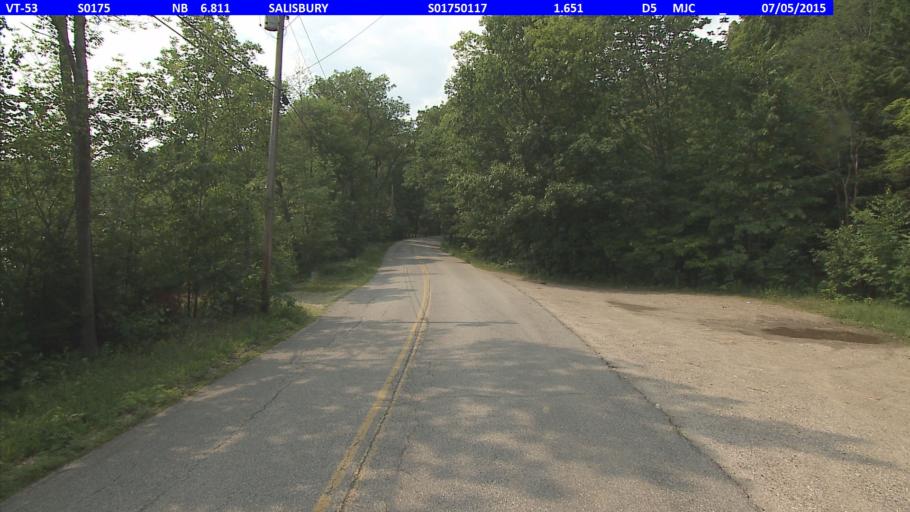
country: US
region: Vermont
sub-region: Rutland County
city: Brandon
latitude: 43.9207
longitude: -73.0715
